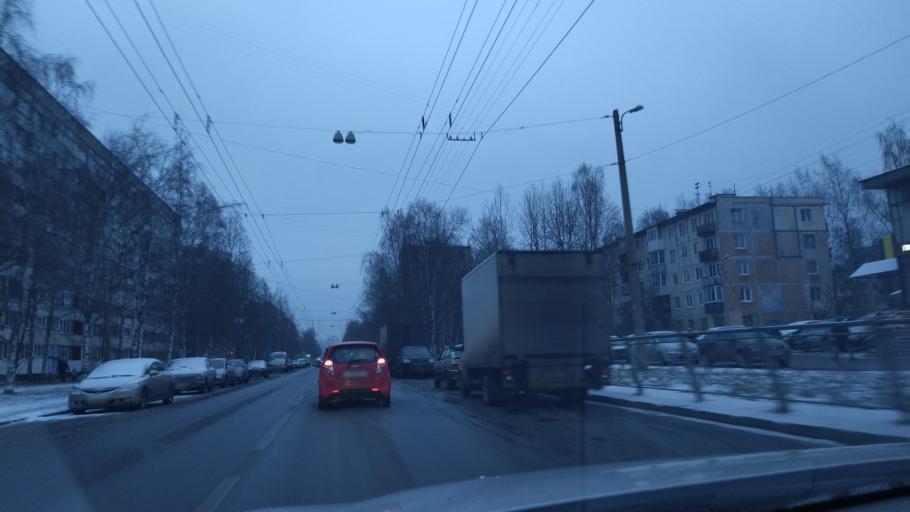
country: RU
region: Leningrad
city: Akademicheskoe
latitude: 60.0126
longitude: 30.4107
